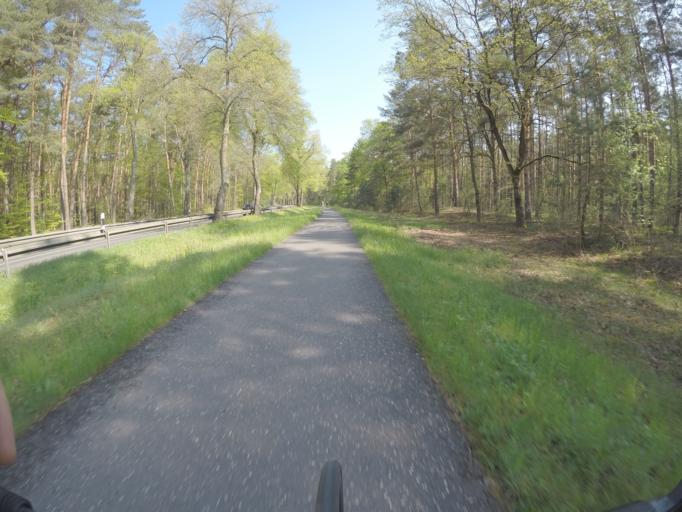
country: DE
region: Brandenburg
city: Wandlitz
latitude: 52.6940
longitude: 13.4430
